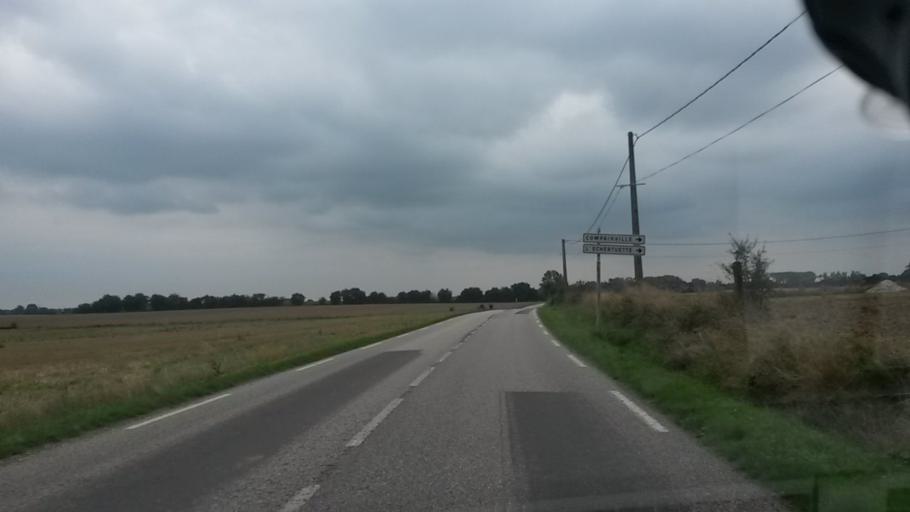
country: FR
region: Haute-Normandie
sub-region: Departement de la Seine-Maritime
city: Gaillefontaine
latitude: 49.6854
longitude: 1.6322
